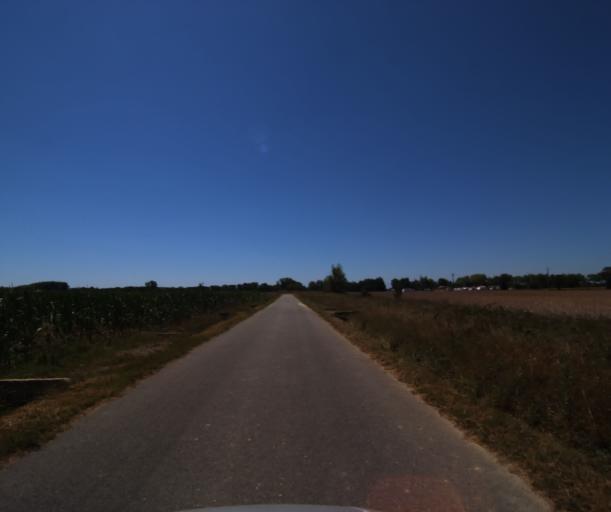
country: FR
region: Midi-Pyrenees
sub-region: Departement de la Haute-Garonne
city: Seysses
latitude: 43.4691
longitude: 1.2961
